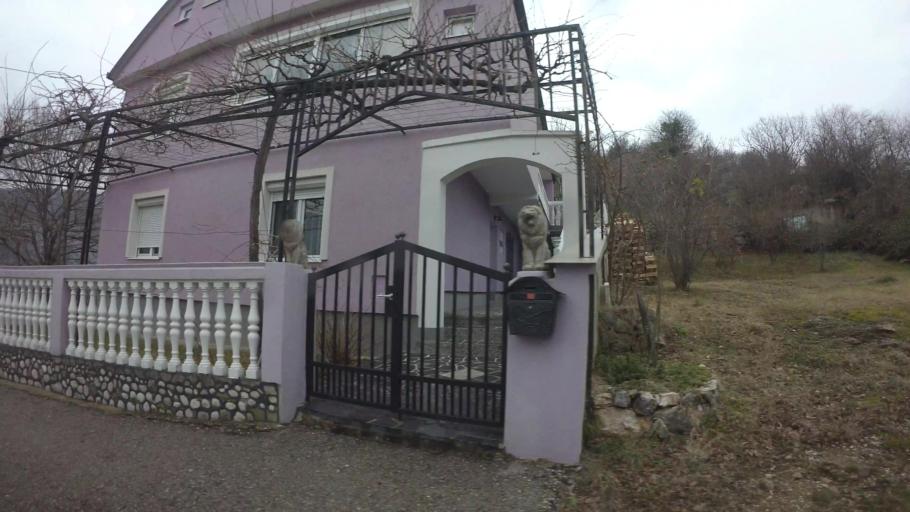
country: BA
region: Federation of Bosnia and Herzegovina
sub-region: Hercegovacko-Bosanski Kanton
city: Mostar
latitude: 43.3610
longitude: 17.8175
